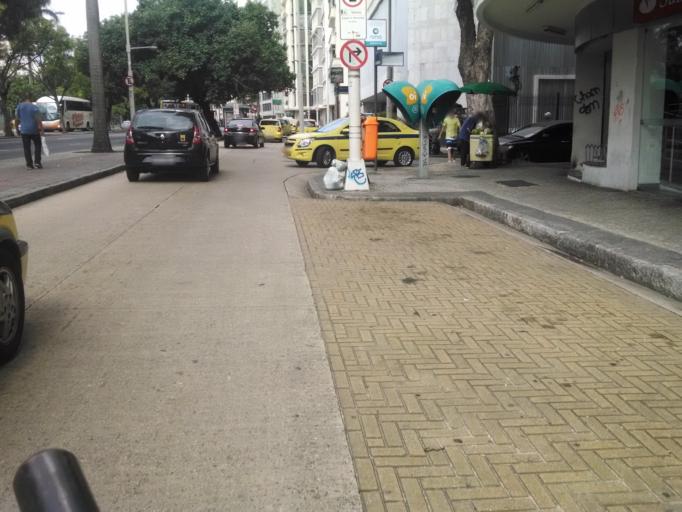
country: BR
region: Rio de Janeiro
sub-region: Rio De Janeiro
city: Rio de Janeiro
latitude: -22.9318
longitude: -43.1746
